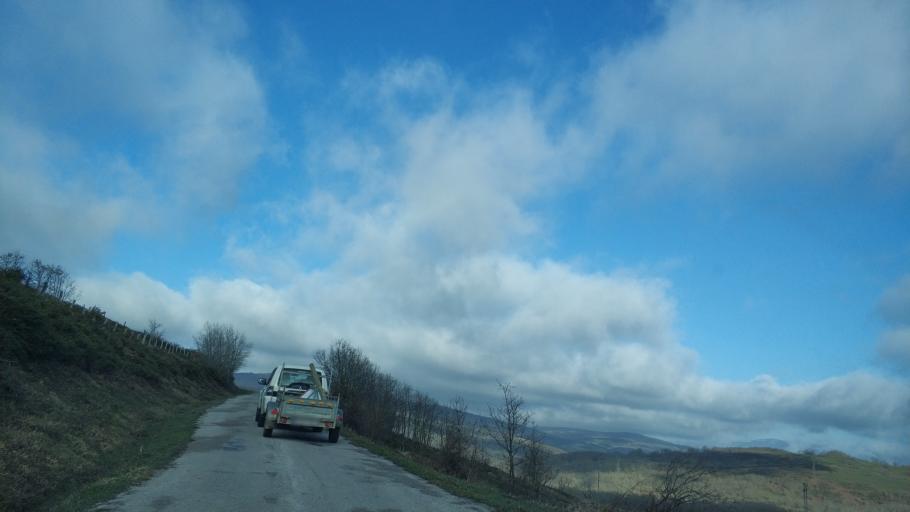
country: ES
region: Castille and Leon
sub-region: Provincia de Burgos
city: Arija
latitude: 42.9104
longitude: -4.0043
